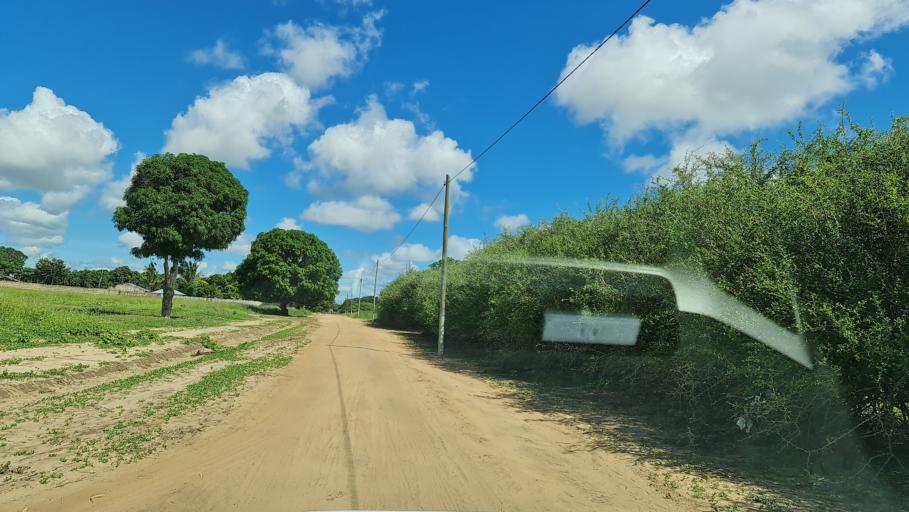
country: MZ
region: Nampula
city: Ilha de Mocambique
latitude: -15.5586
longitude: 40.4142
